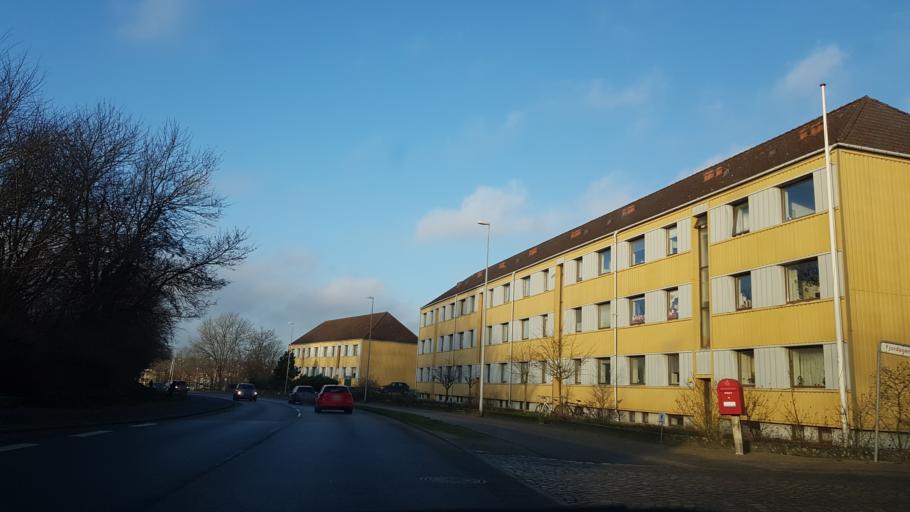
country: DK
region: South Denmark
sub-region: Haderslev Kommune
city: Haderslev
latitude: 55.2452
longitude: 9.5029
